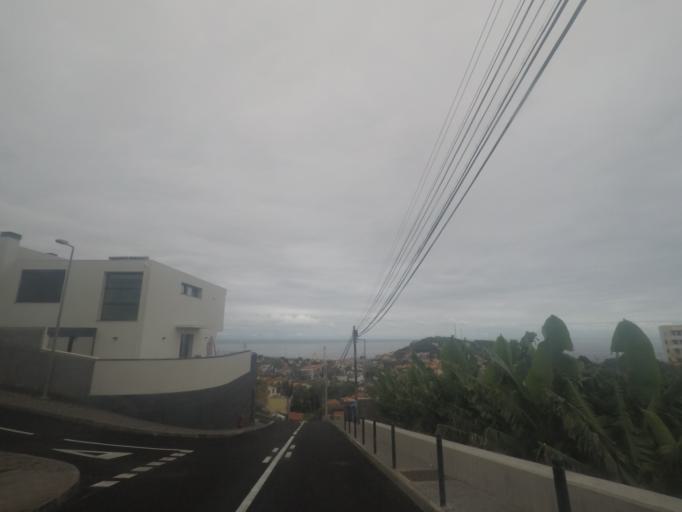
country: PT
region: Madeira
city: Camara de Lobos
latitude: 32.6604
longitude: -16.9717
